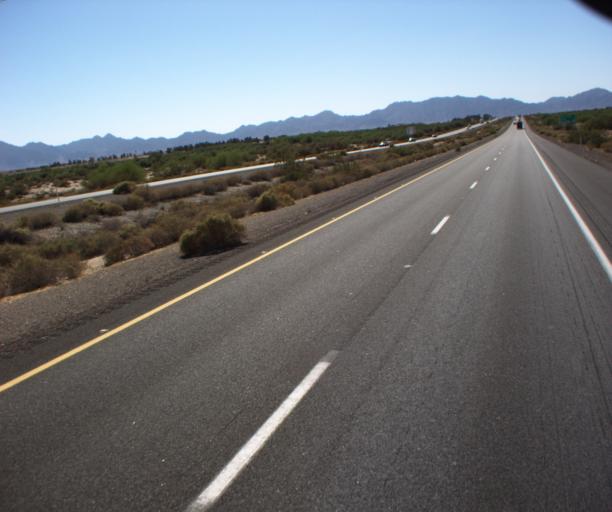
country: US
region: Arizona
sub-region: Yuma County
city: Wellton
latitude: 32.6583
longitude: -114.1580
